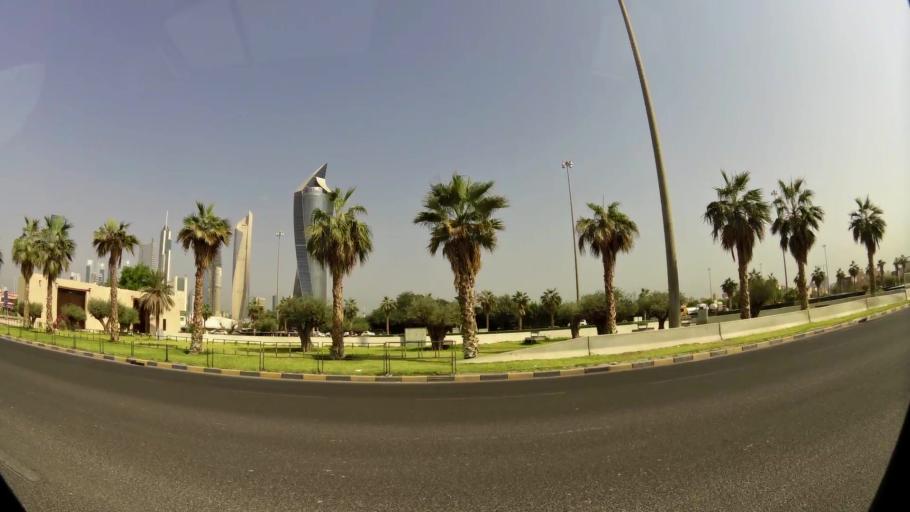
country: KW
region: Al Asimah
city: Ad Dasmah
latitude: 29.3656
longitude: 47.9906
